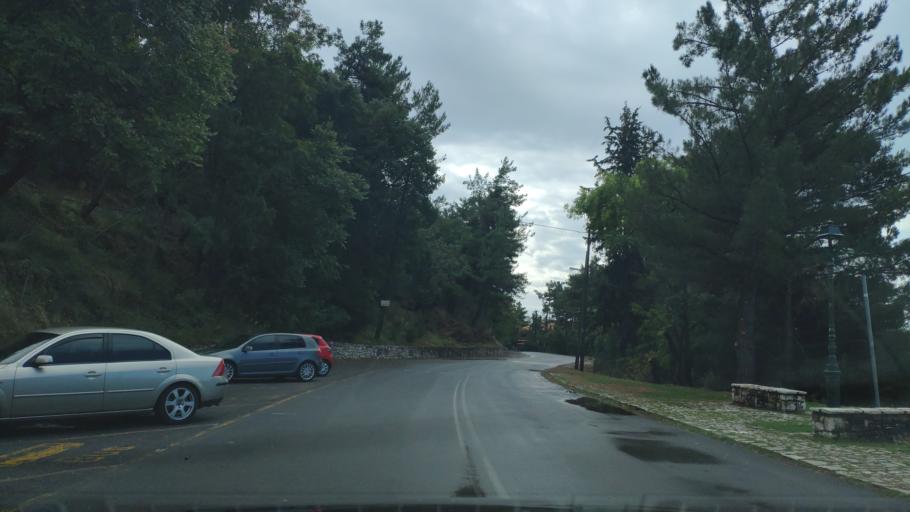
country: GR
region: Peloponnese
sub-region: Nomos Arkadias
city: Dimitsana
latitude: 37.5918
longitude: 22.0426
